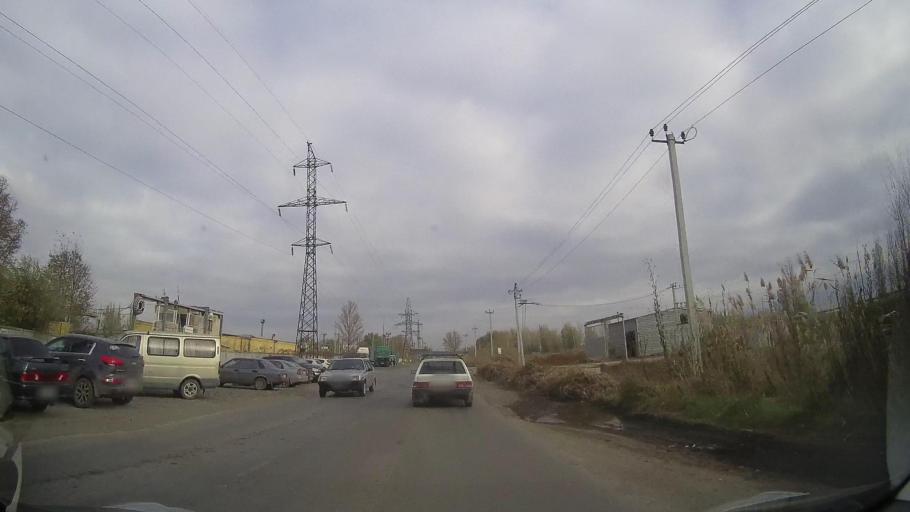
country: RU
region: Rostov
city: Bataysk
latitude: 47.1077
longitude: 39.7637
